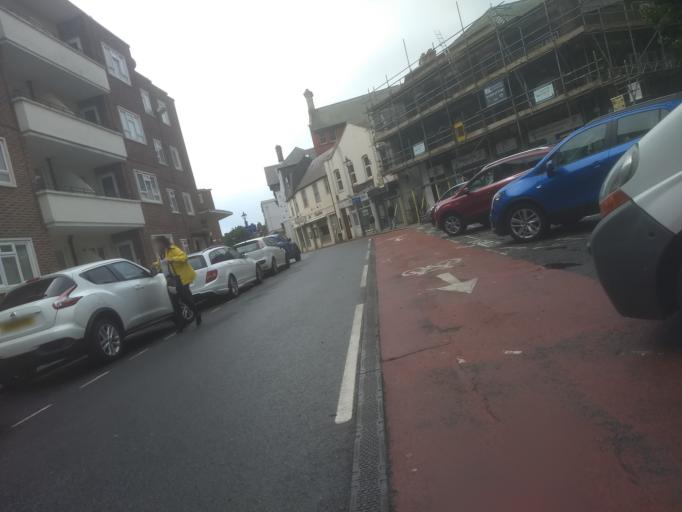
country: GB
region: England
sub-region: Kent
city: Dover
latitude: 51.1259
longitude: 1.3138
